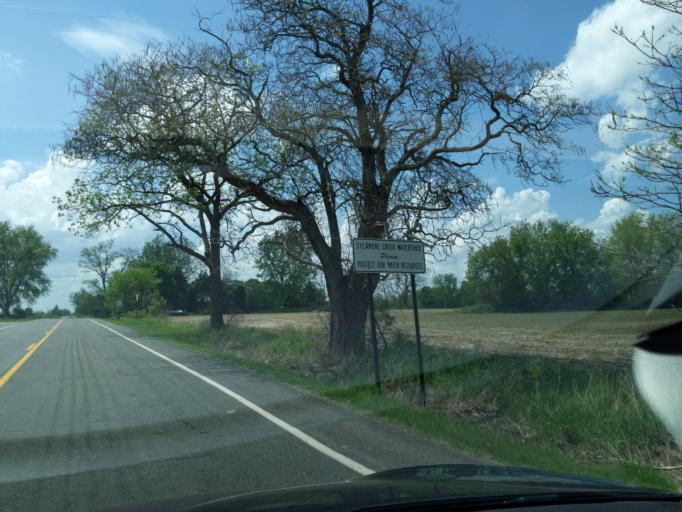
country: US
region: Michigan
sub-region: Ingham County
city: Mason
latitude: 42.5963
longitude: -84.3730
